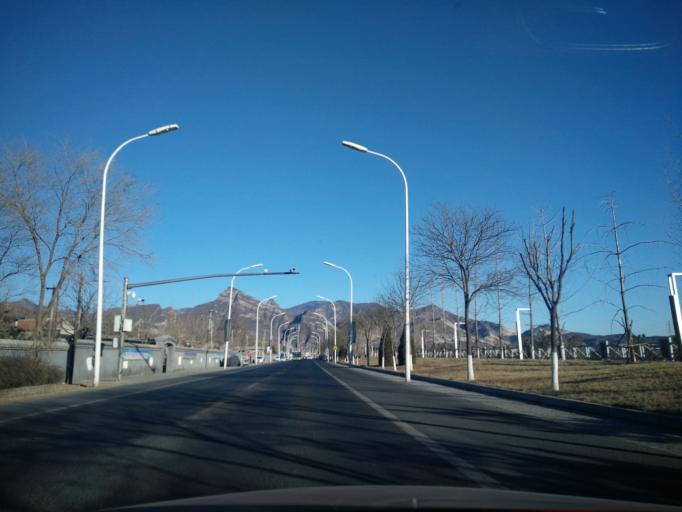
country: CN
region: Beijing
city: Junzhuang
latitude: 39.9794
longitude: 116.0831
